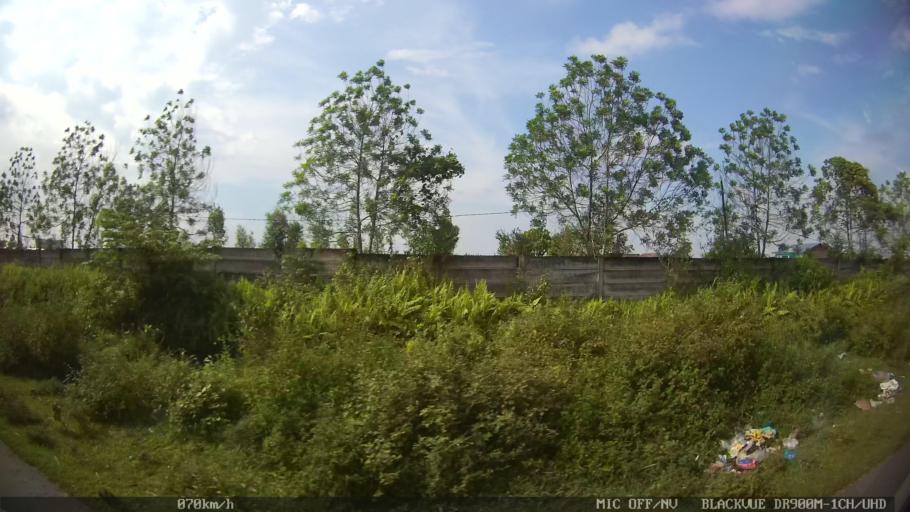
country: ID
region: North Sumatra
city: Medan
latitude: 3.5731
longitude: 98.7622
